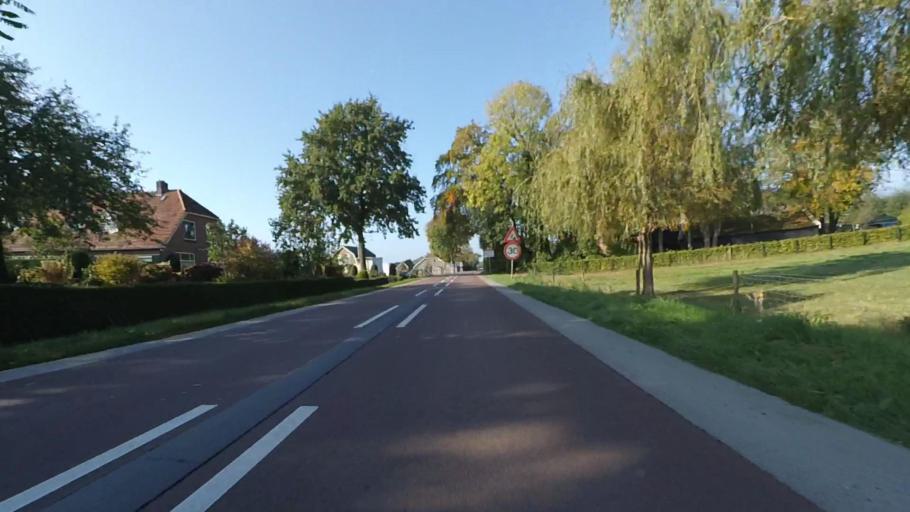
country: NL
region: Gelderland
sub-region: Gemeente Ermelo
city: Horst
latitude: 52.2641
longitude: 5.5477
